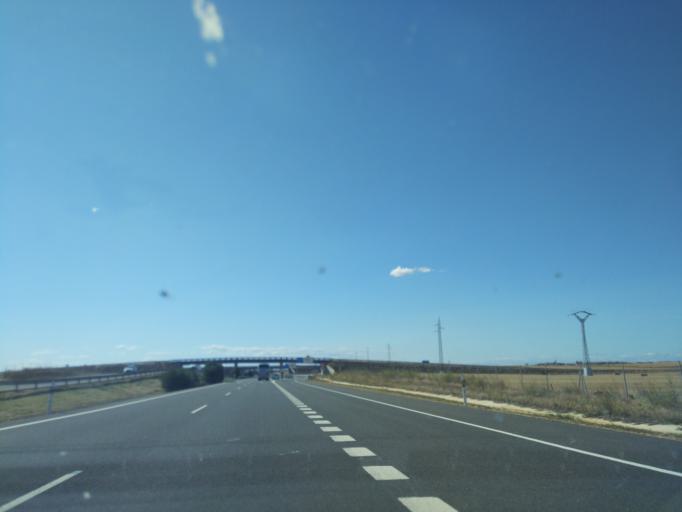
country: ES
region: Castille and Leon
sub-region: Provincia de Zamora
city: Castrogonzalo
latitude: 41.9627
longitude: -5.5859
